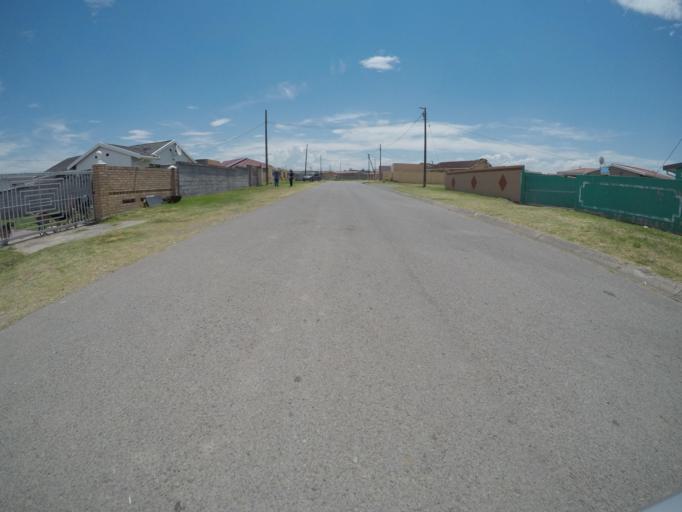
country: ZA
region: Eastern Cape
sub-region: Buffalo City Metropolitan Municipality
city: East London
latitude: -33.0490
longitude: 27.8504
